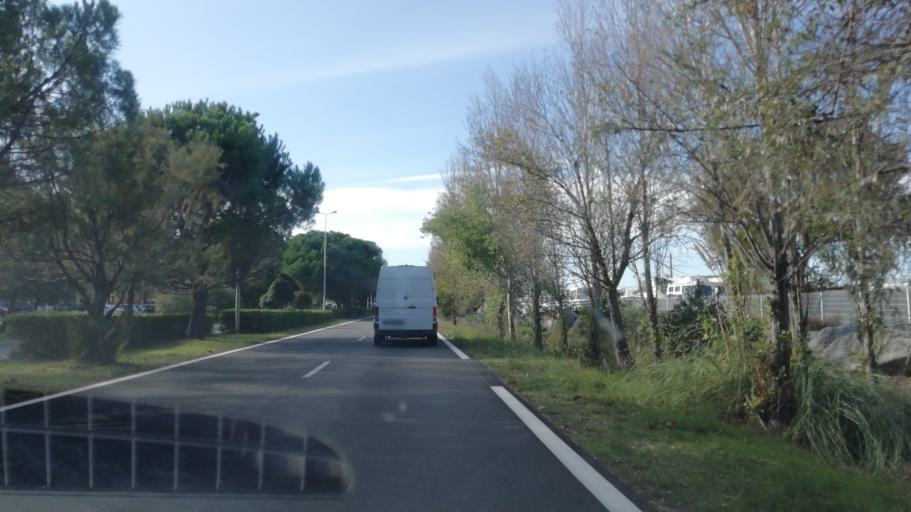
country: FR
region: Languedoc-Roussillon
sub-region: Departement de l'Herault
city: Perols
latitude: 43.5488
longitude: 3.9764
